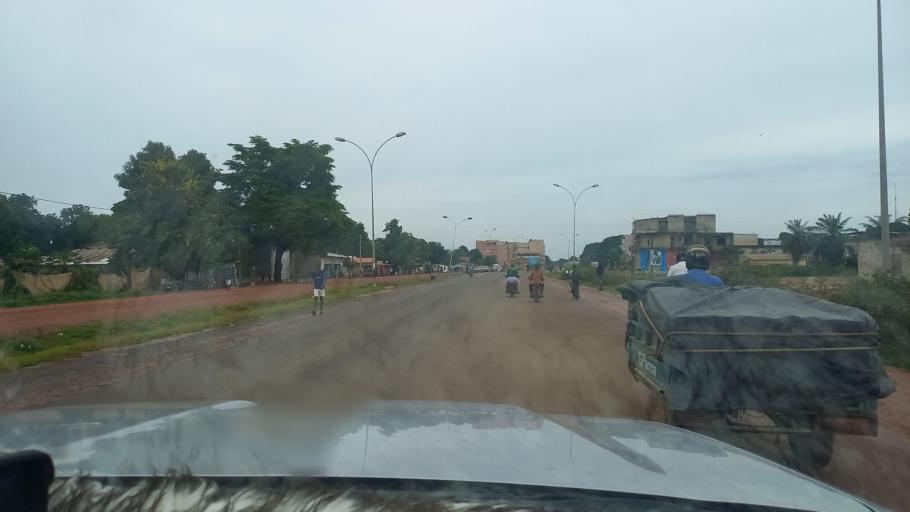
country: SN
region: Ziguinchor
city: Ziguinchor
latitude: 12.5563
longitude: -16.2664
